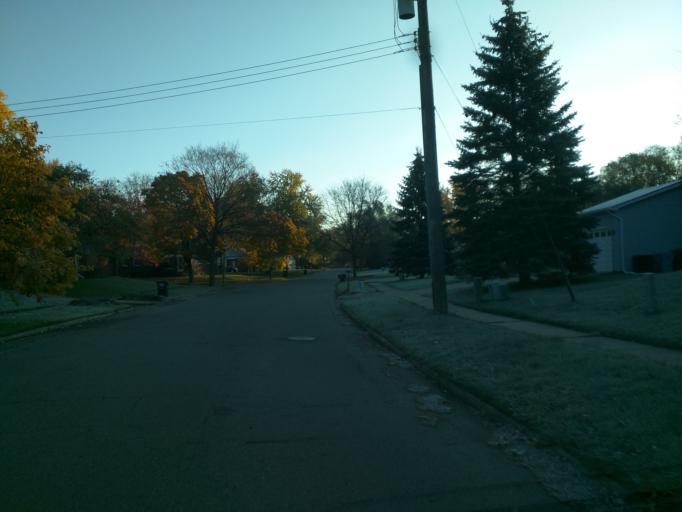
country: US
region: Michigan
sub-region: Ingham County
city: Edgemont Park
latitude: 42.7562
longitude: -84.5863
